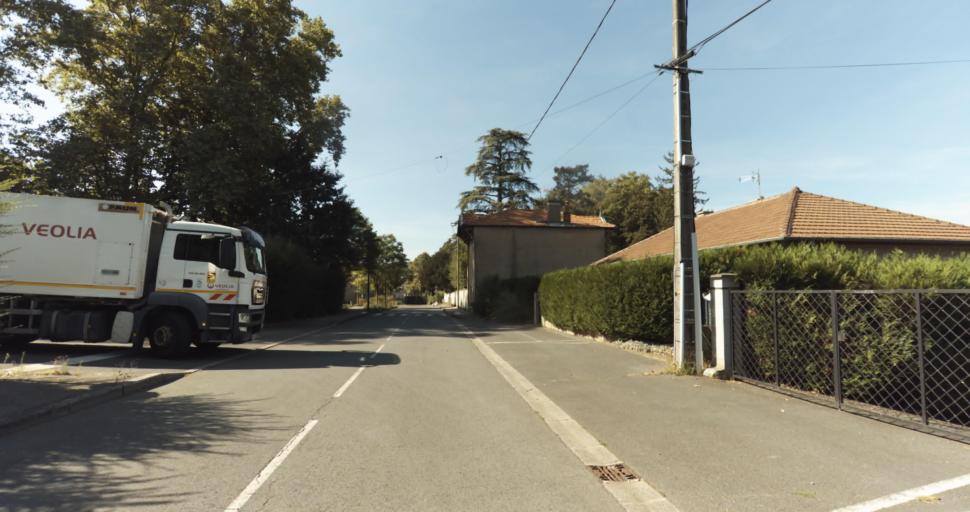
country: FR
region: Rhone-Alpes
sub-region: Departement du Rhone
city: Neuville-sur-Saone
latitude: 45.8777
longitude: 4.8460
